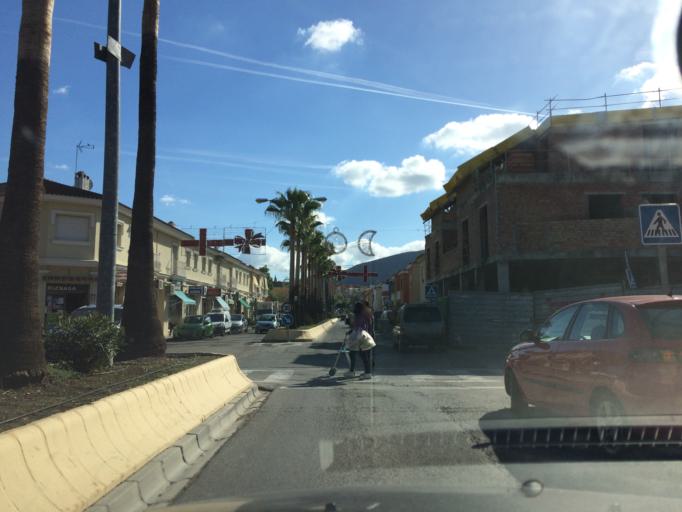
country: ES
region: Andalusia
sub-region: Provincia de Malaga
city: Estacion de Cartama
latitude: 36.7368
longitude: -4.6138
